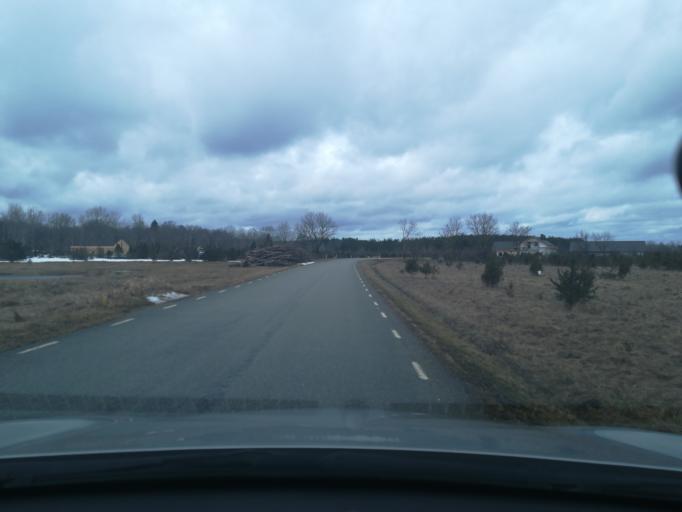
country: EE
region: Harju
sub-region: Saue linn
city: Saue
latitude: 59.3583
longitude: 24.5298
